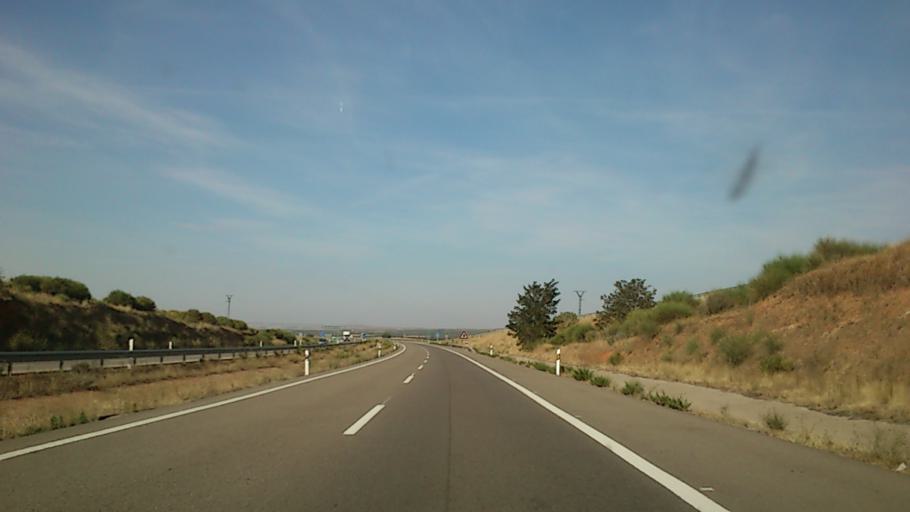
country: ES
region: Aragon
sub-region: Provincia de Zaragoza
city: Paniza
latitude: 41.2991
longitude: -1.2161
